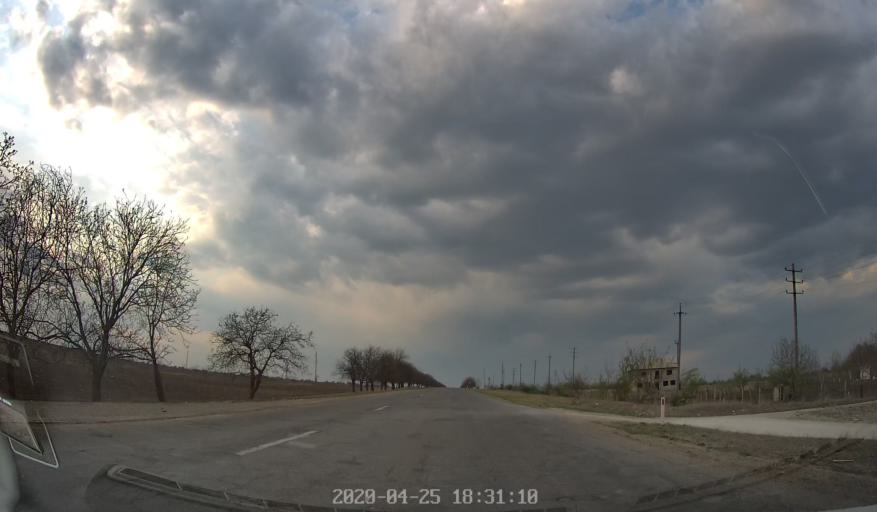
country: MD
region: Criuleni
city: Criuleni
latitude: 47.2144
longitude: 29.1482
